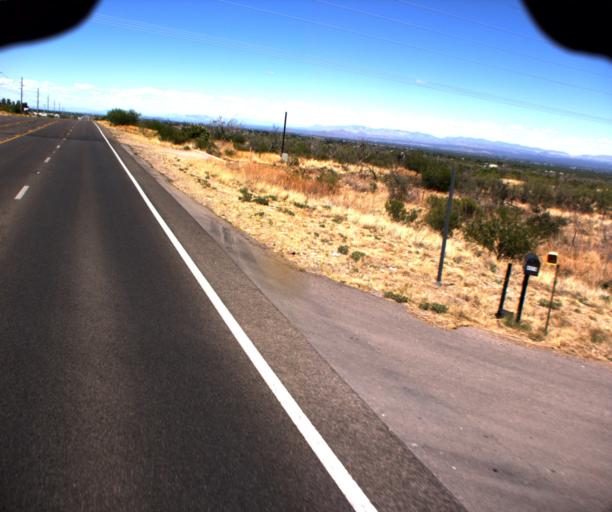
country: US
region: Arizona
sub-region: Cochise County
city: Sierra Vista Southeast
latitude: 31.4524
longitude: -110.2574
